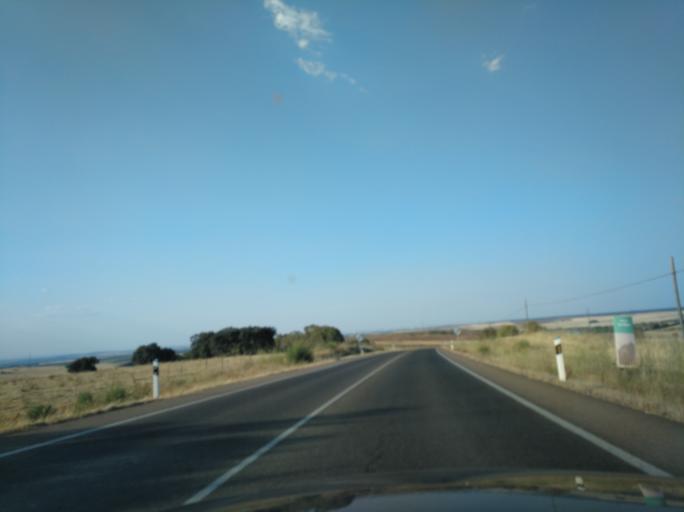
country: ES
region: Extremadura
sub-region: Provincia de Badajoz
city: Olivenza
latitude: 38.7189
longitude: -7.0836
